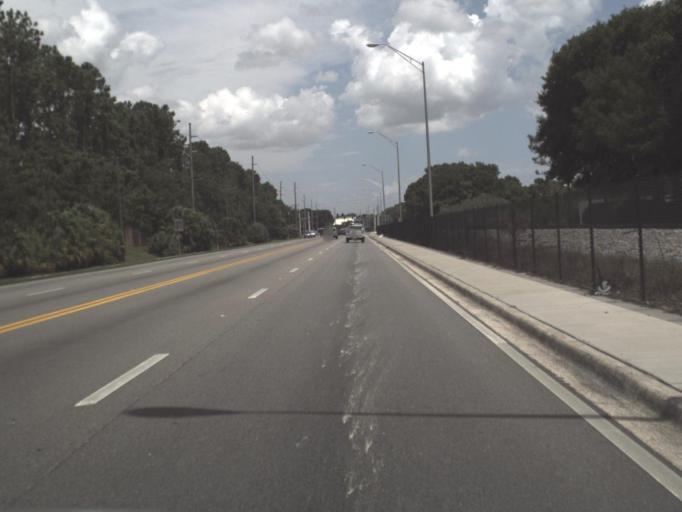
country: US
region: Florida
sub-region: Hillsborough County
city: Carrollwood
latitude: 28.0360
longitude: -82.4963
